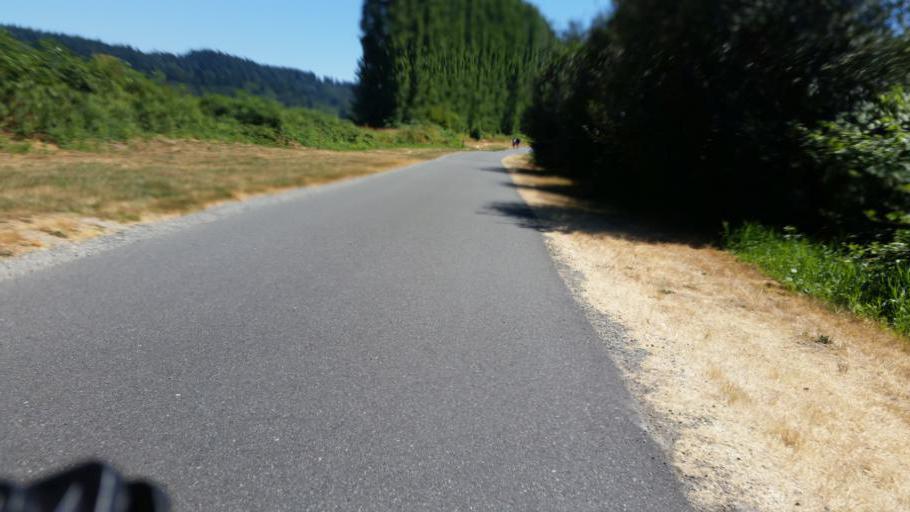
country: US
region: Washington
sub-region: King County
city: Woodinville
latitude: 47.7479
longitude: -122.1611
